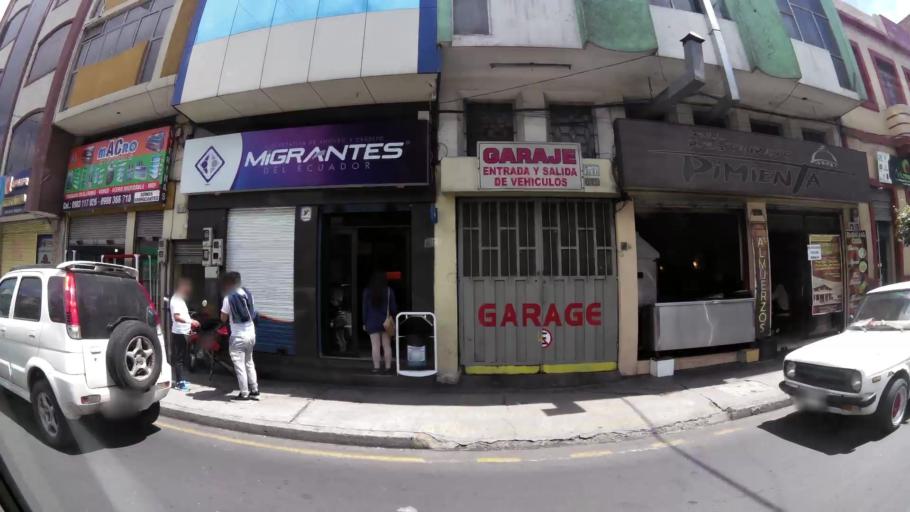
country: EC
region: Tungurahua
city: Ambato
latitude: -1.2383
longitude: -78.6227
